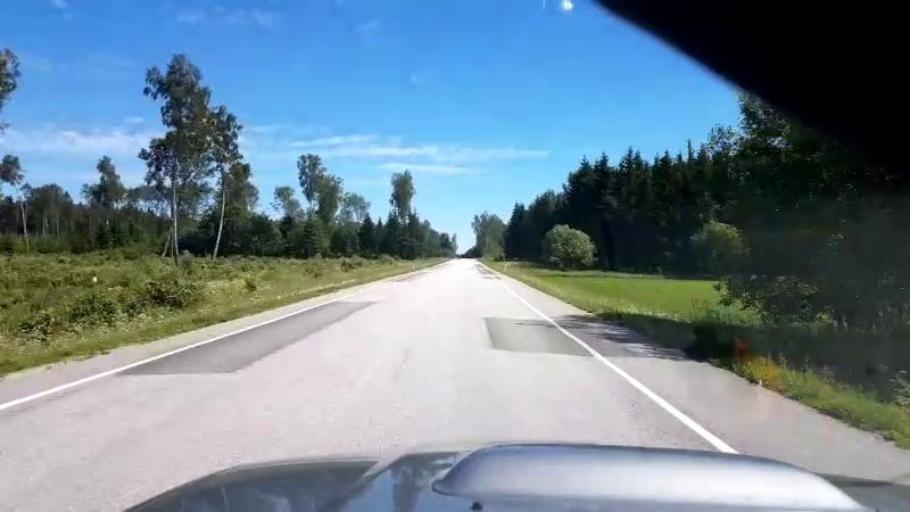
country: EE
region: Jaervamaa
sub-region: Jaerva-Jaani vald
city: Jarva-Jaani
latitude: 58.9950
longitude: 25.9528
